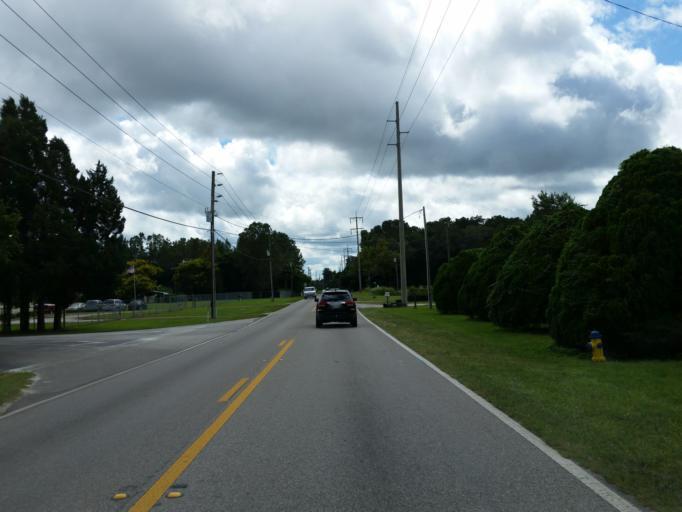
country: US
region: Florida
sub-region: Pasco County
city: Zephyrhills West
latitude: 28.2108
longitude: -82.2461
